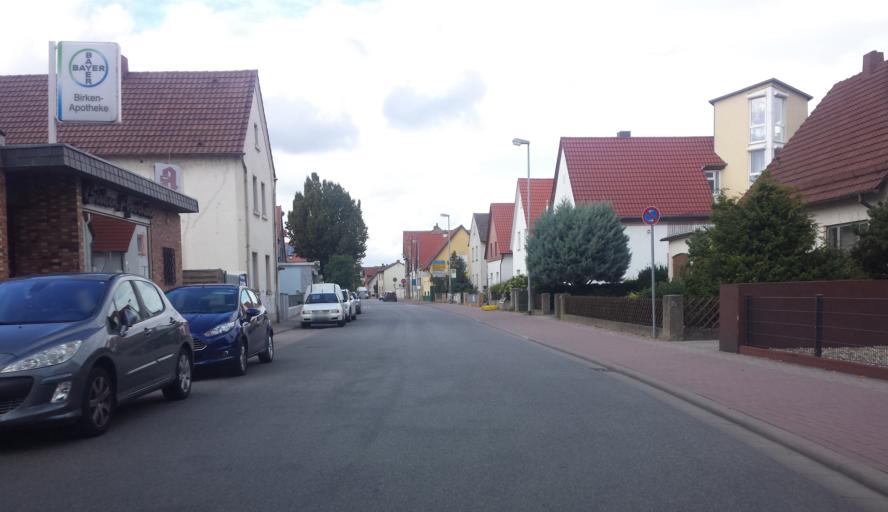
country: DE
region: Rheinland-Pfalz
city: Dannstadt-Schauernheim
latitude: 49.4310
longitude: 8.3120
